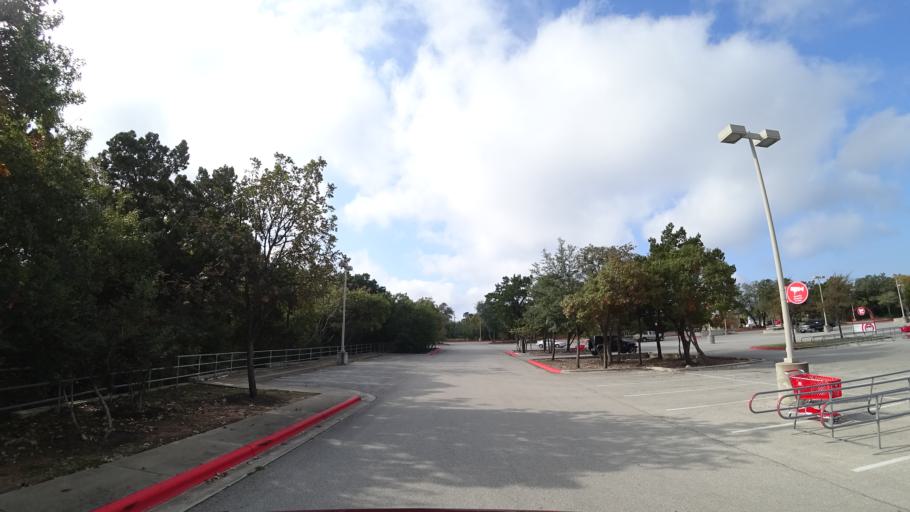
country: US
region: Texas
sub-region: Williamson County
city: Anderson Mill
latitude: 30.4016
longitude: -97.8500
